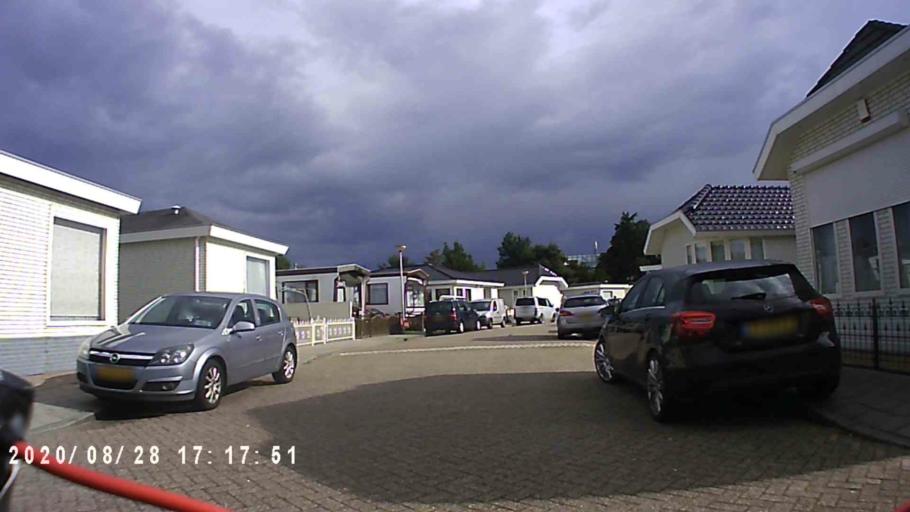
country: NL
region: Groningen
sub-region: Gemeente Groningen
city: Groningen
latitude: 53.2013
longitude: 6.5230
